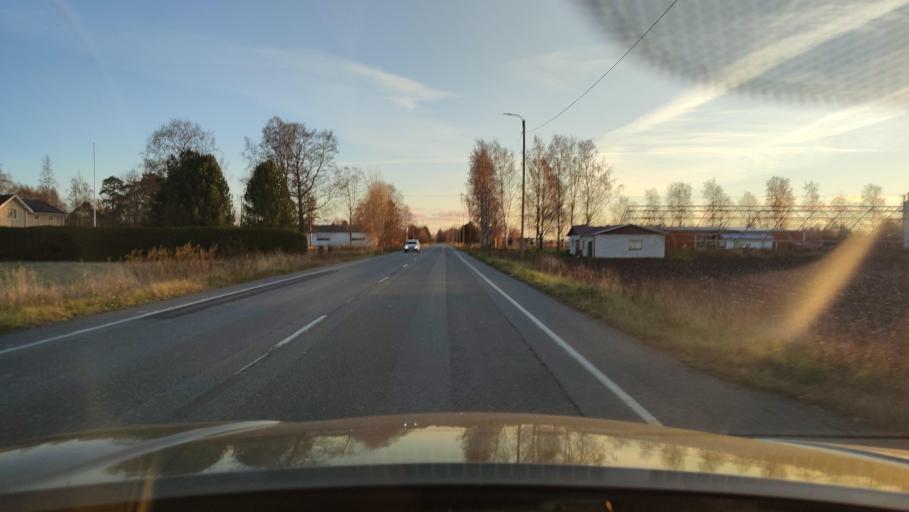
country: FI
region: Ostrobothnia
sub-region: Sydosterbotten
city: Naerpes
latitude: 62.4594
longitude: 21.3555
